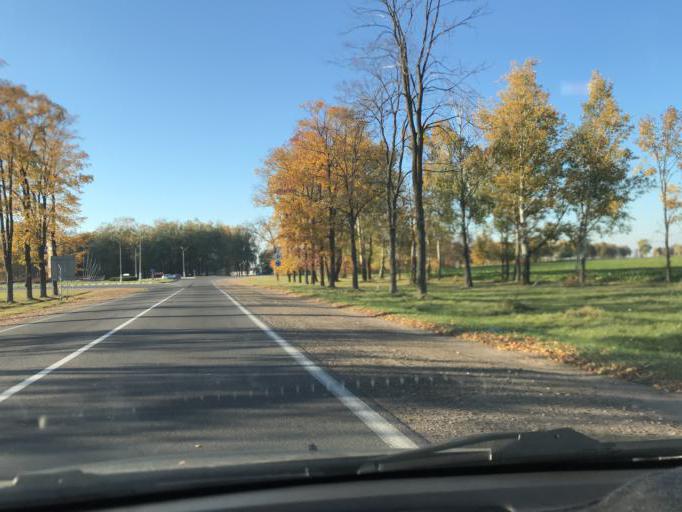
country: BY
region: Minsk
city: Slutsk
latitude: 53.0516
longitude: 27.5566
